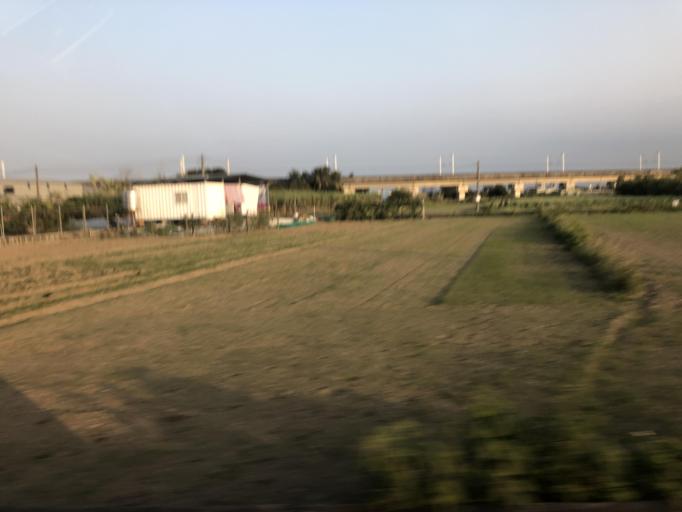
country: TW
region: Taiwan
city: Xinying
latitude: 23.1525
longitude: 120.2754
